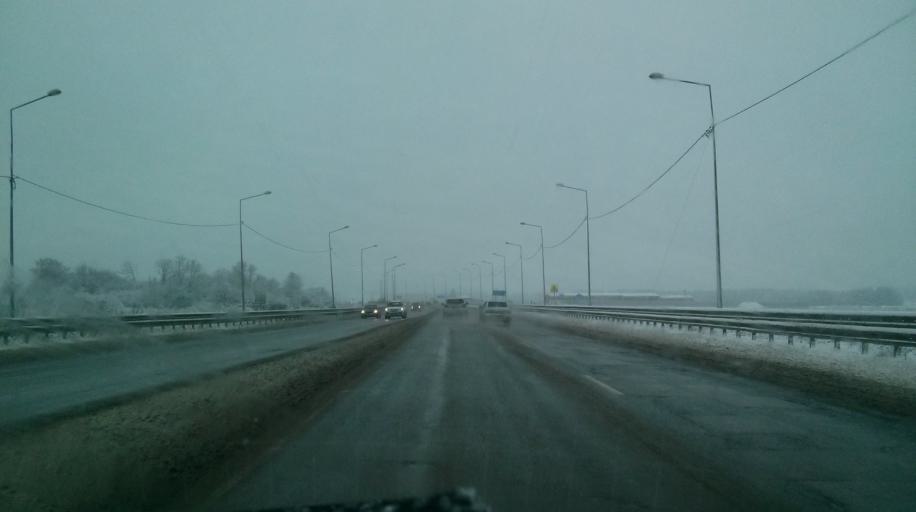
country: RU
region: Nizjnij Novgorod
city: Burevestnik
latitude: 56.1705
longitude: 43.7408
